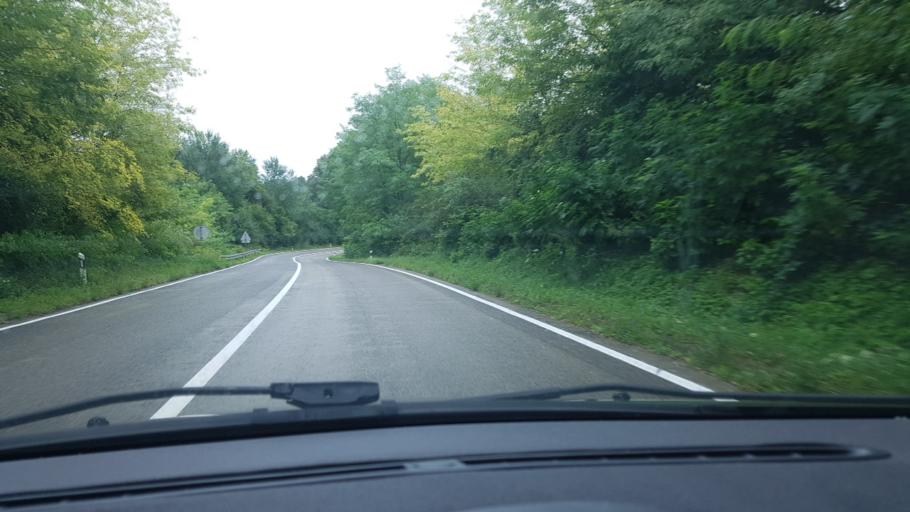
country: SI
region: Crnomelj
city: Crnomelj
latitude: 45.4508
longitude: 15.3072
